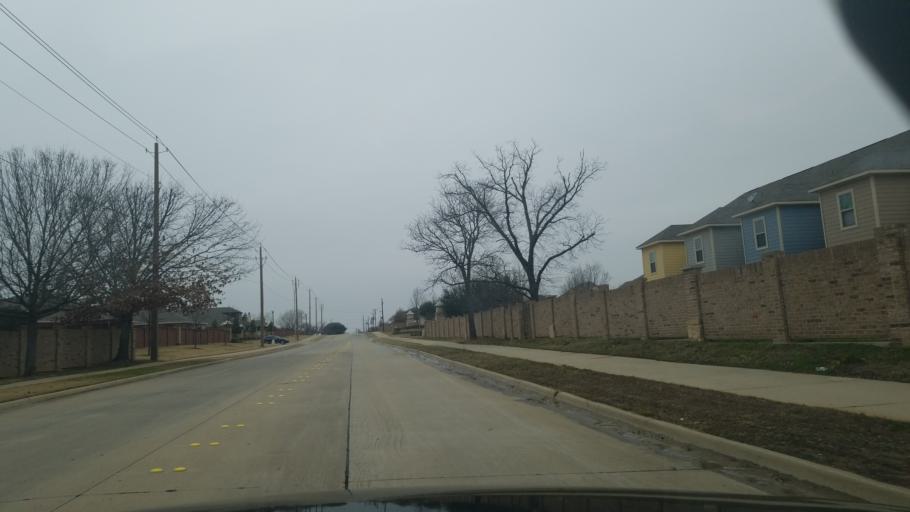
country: US
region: Texas
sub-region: Denton County
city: Corinth
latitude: 33.1710
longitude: -97.0763
